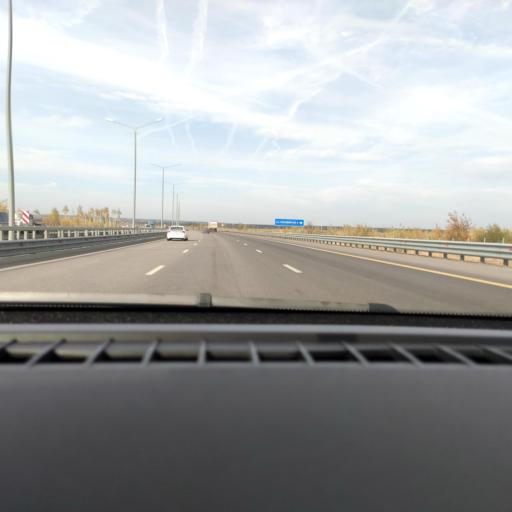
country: RU
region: Voronezj
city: Somovo
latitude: 51.7630
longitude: 39.3060
